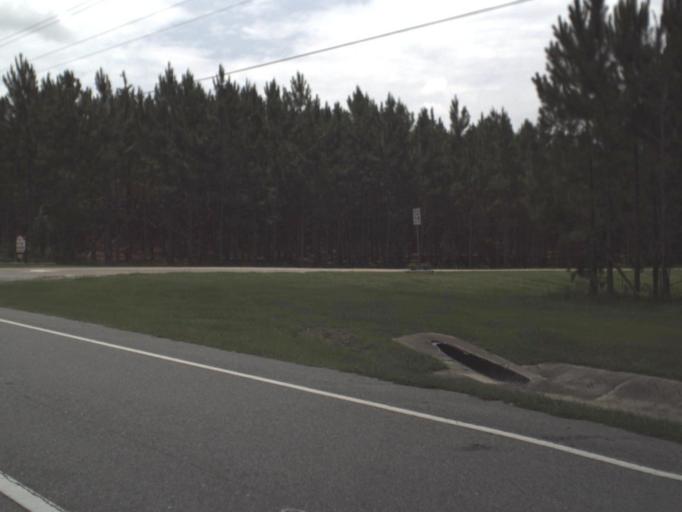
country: US
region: Florida
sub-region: Madison County
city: Madison
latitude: 30.4862
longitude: -83.4566
